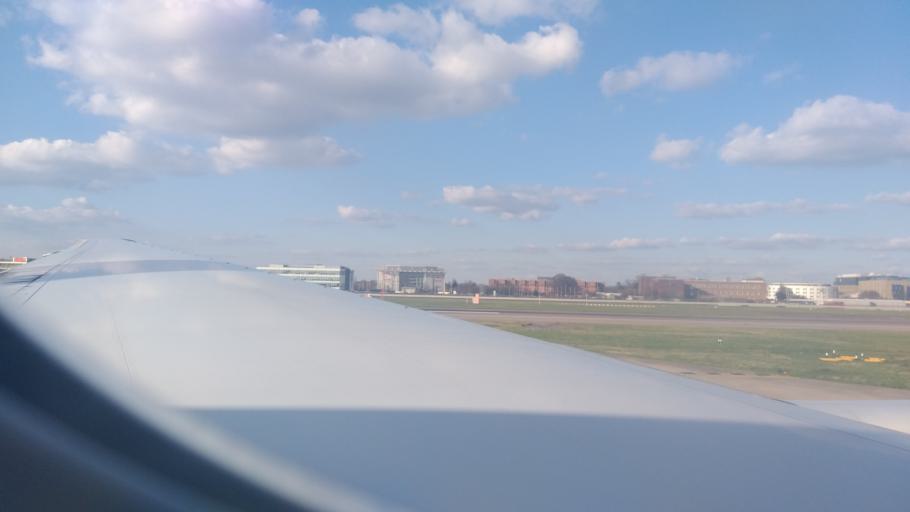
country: GB
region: England
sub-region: Greater London
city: West Drayton
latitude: 51.4760
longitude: -0.4378
